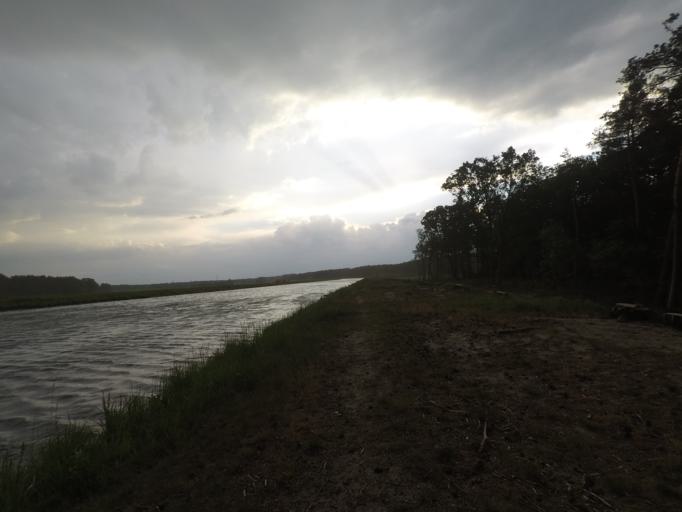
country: DE
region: Brandenburg
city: Melchow
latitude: 52.8608
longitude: 13.7067
